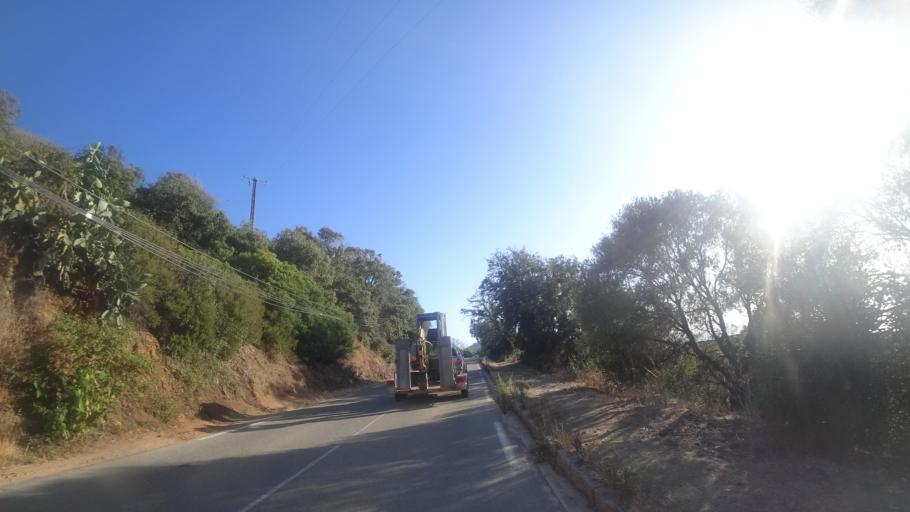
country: FR
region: Corsica
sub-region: Departement de la Corse-du-Sud
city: Cargese
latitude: 42.1429
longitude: 8.6025
